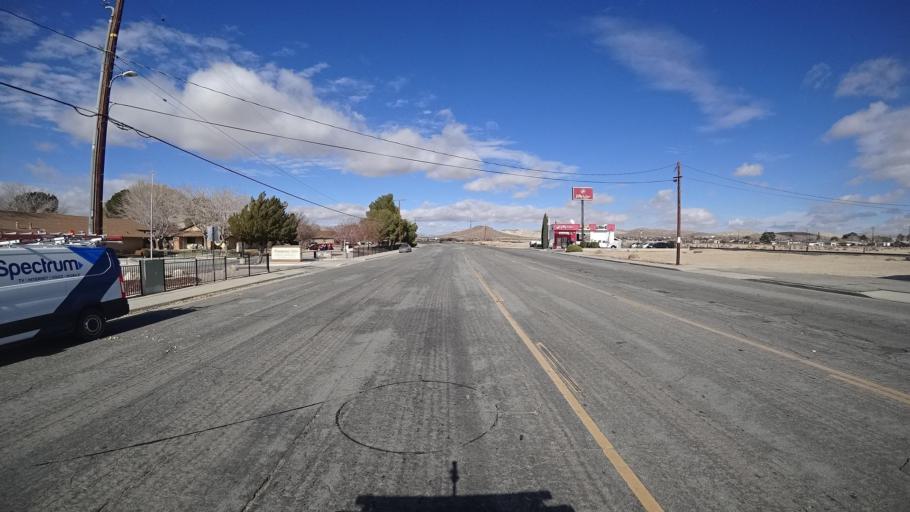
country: US
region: California
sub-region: Kern County
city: Rosamond
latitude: 34.8651
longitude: -118.1632
